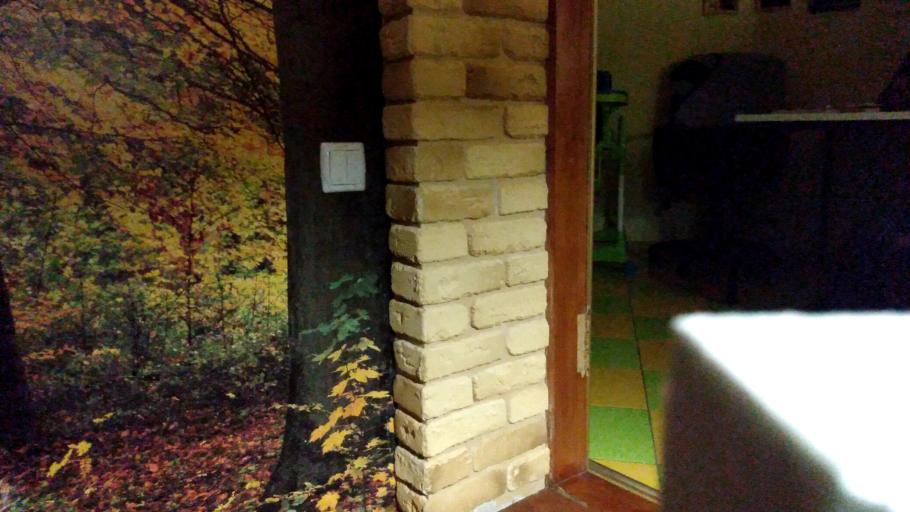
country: RU
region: Arkhangelskaya
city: Kargopol'
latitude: 61.3960
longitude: 37.8178
